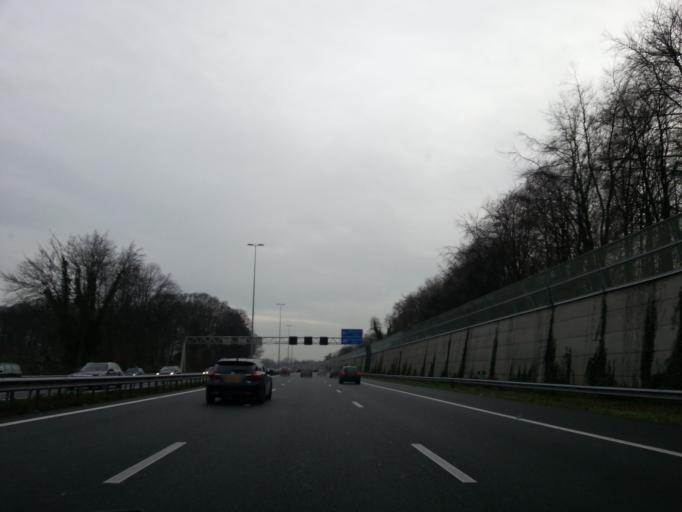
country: NL
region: Gelderland
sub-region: Gemeente Rozendaal
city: Rozendaal
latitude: 51.9987
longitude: 5.9513
